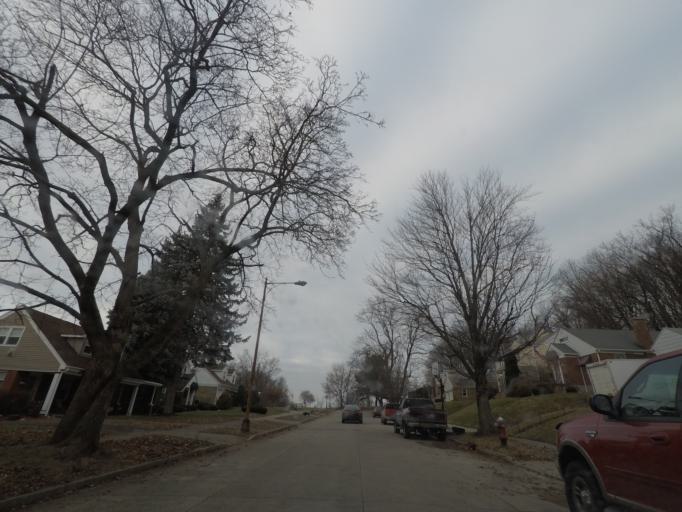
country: US
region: New York
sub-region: Albany County
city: Green Island
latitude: 42.7428
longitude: -73.6665
